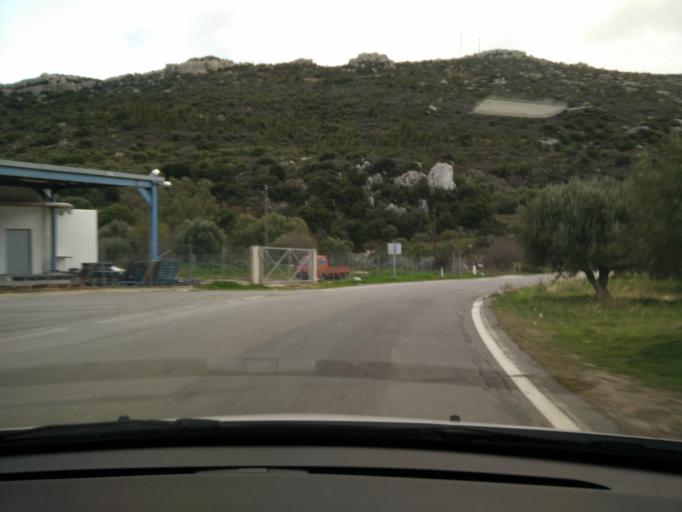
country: GR
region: Crete
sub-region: Nomos Lasithiou
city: Gra Liyia
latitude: 35.0818
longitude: 25.7106
